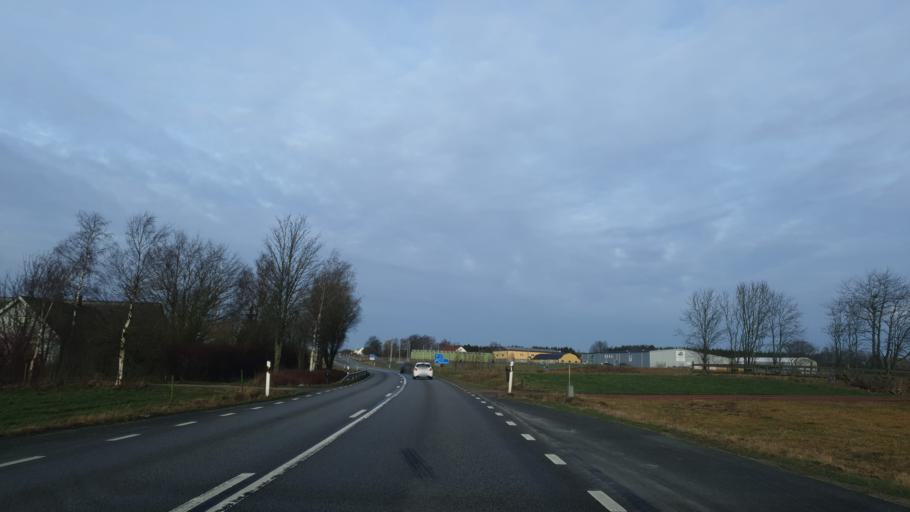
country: SE
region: Skane
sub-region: Horby Kommun
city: Hoerby
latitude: 55.7878
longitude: 13.6770
